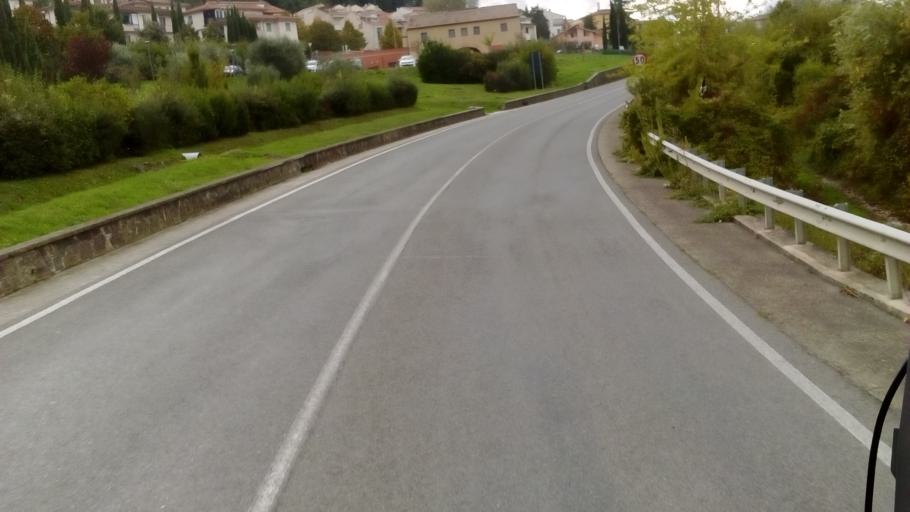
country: IT
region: Tuscany
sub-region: Province of Florence
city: Montespertoli
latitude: 43.6464
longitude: 11.0800
